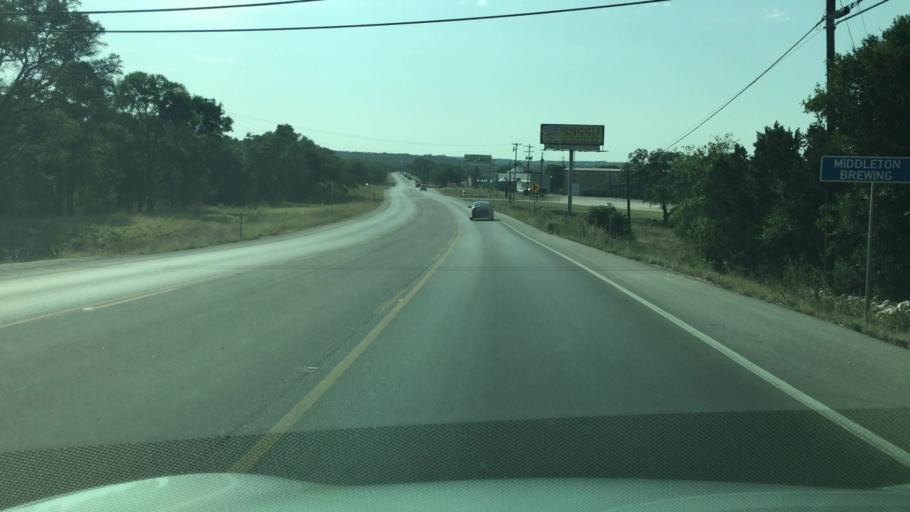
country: US
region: Texas
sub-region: Hays County
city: Wimberley
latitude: 29.9288
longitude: -98.0687
